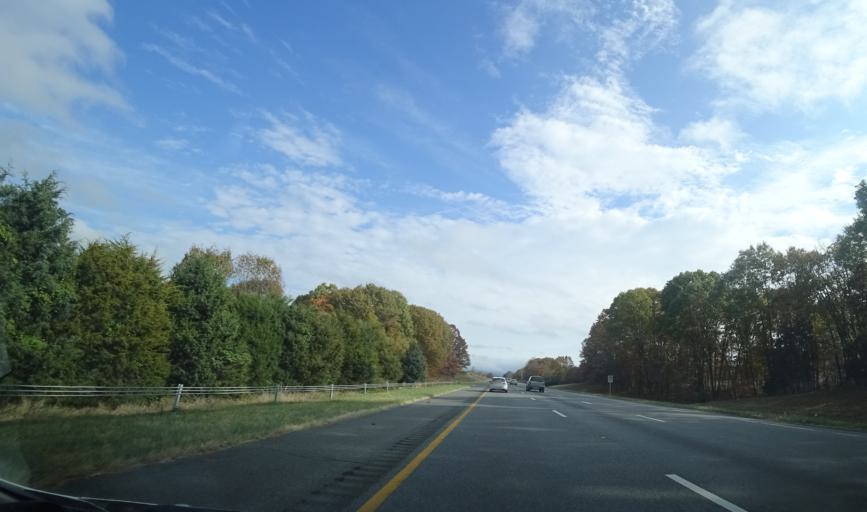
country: US
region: Virginia
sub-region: Frederick County
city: Middletown
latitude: 38.9809
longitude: -78.2281
